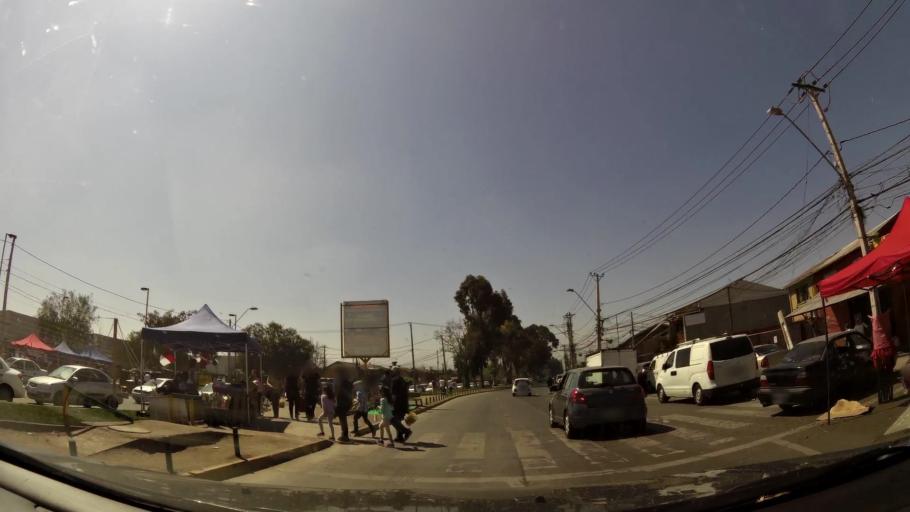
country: CL
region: Santiago Metropolitan
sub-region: Provincia de Santiago
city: Lo Prado
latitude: -33.3602
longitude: -70.7451
